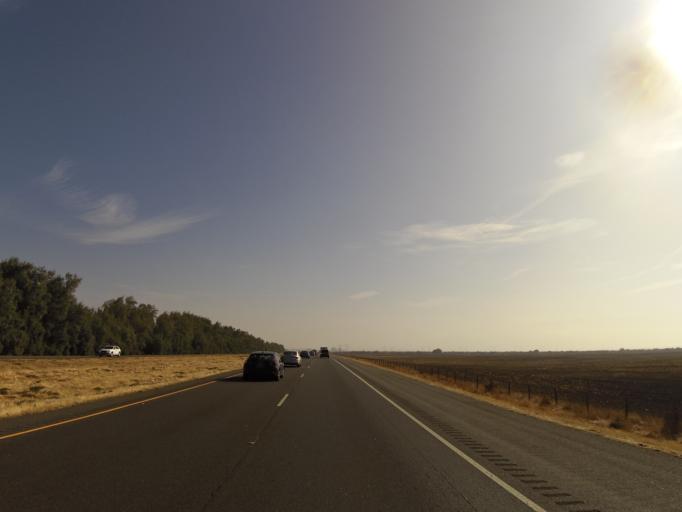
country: US
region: California
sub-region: Kern County
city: Greenfield
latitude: 35.1170
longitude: -119.0618
